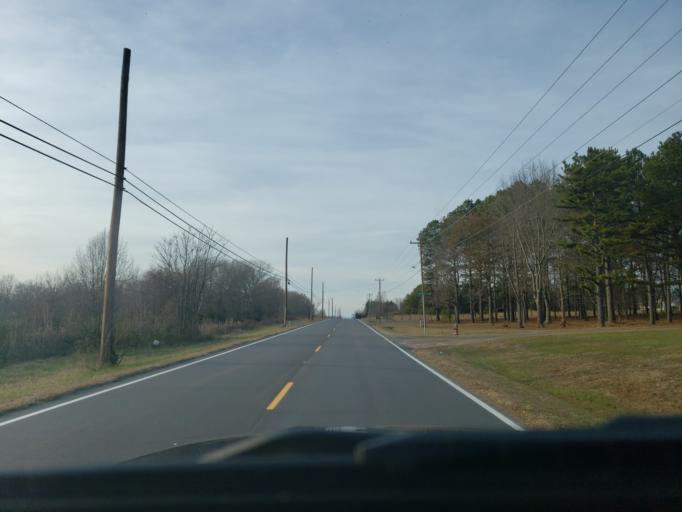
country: US
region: North Carolina
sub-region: Cleveland County
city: Boiling Springs
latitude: 35.3081
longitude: -81.7310
